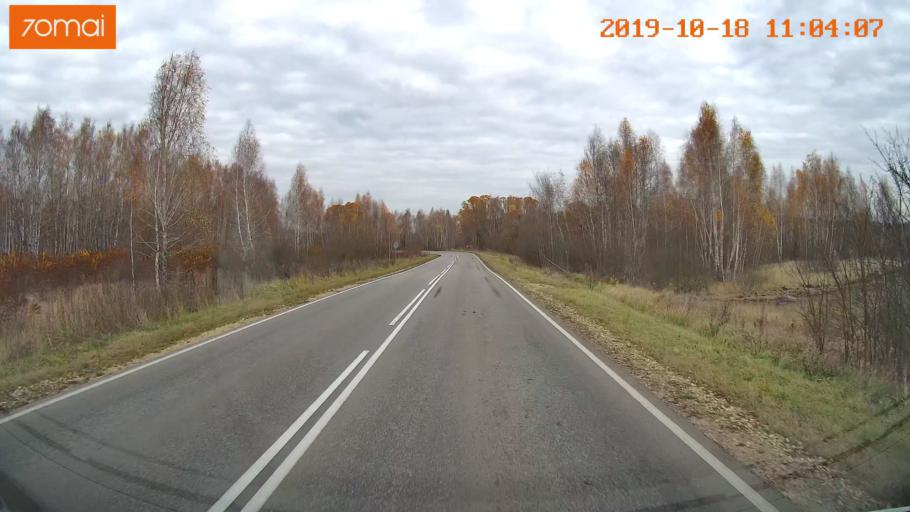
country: RU
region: Tula
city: Yepifan'
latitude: 53.8900
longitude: 38.5504
